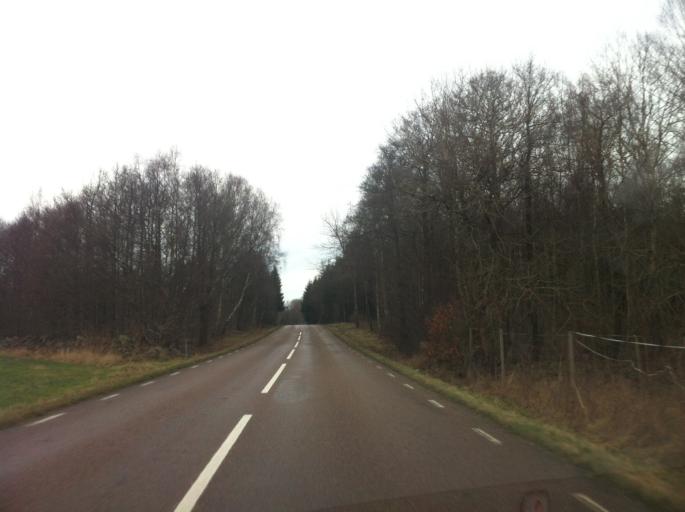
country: SE
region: Skane
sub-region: Svalovs Kommun
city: Kagerod
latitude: 56.0386
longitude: 13.1001
